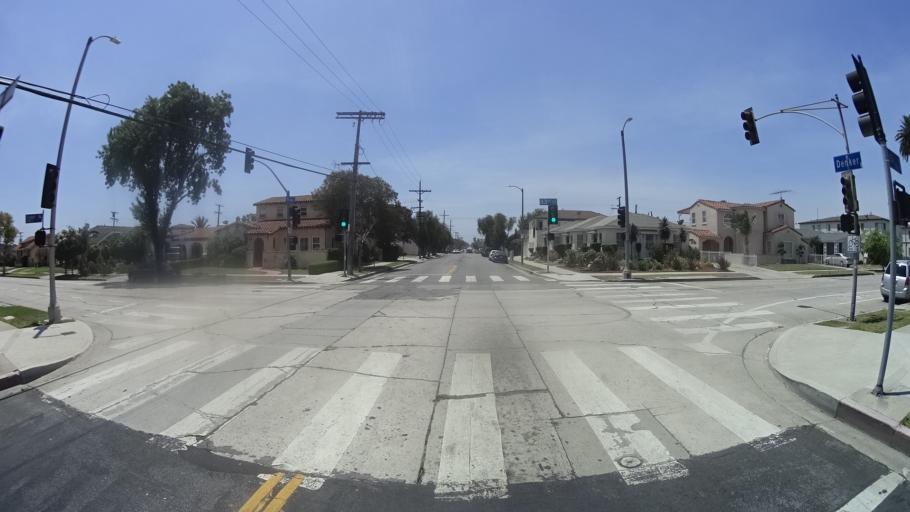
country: US
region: California
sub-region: Los Angeles County
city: Westmont
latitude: 33.9639
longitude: -118.3047
